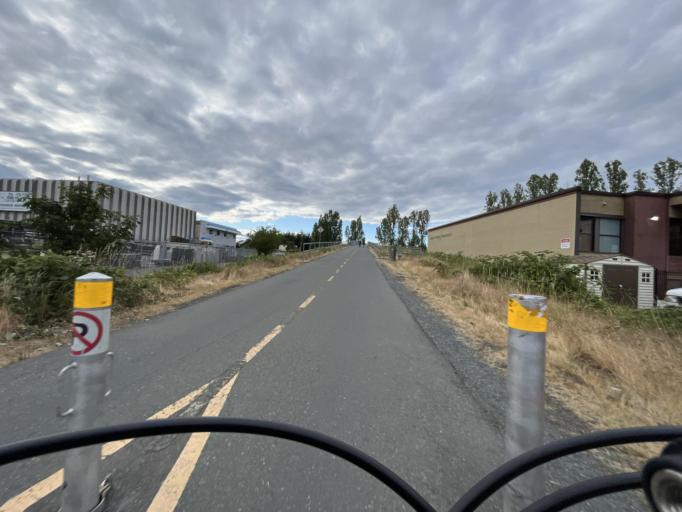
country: CA
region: British Columbia
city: Victoria
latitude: 48.4540
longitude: -123.3773
